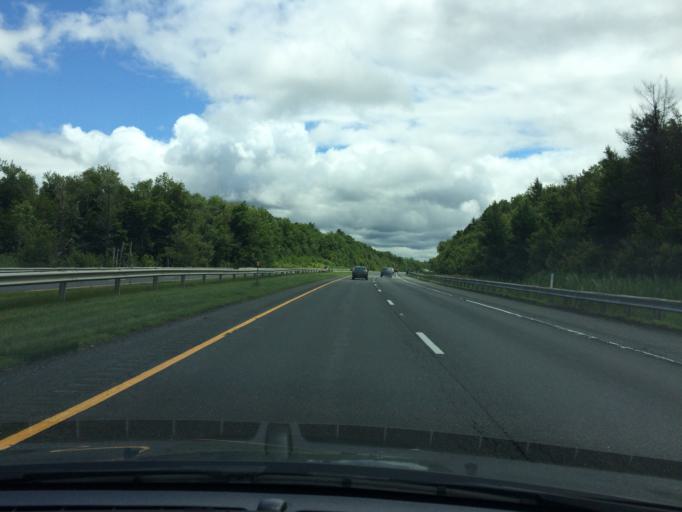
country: US
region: Massachusetts
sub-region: Berkshire County
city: Otis
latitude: 42.2446
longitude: -73.0775
